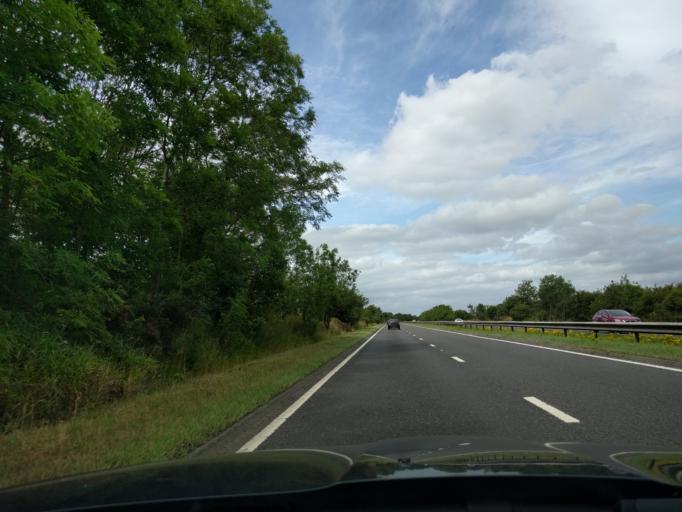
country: GB
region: England
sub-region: Northumberland
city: Morpeth
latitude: 55.1473
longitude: -1.7022
